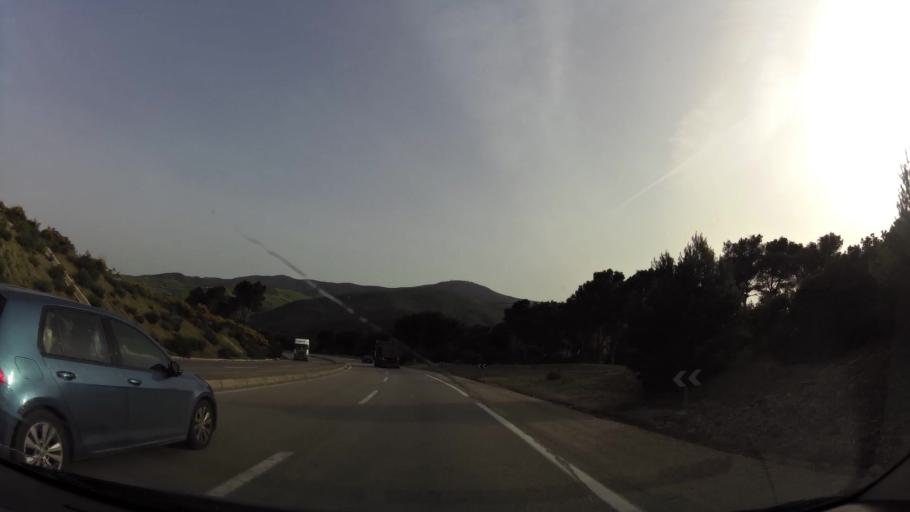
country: MA
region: Tanger-Tetouan
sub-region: Tetouan
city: Saddina
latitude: 35.5512
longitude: -5.5679
